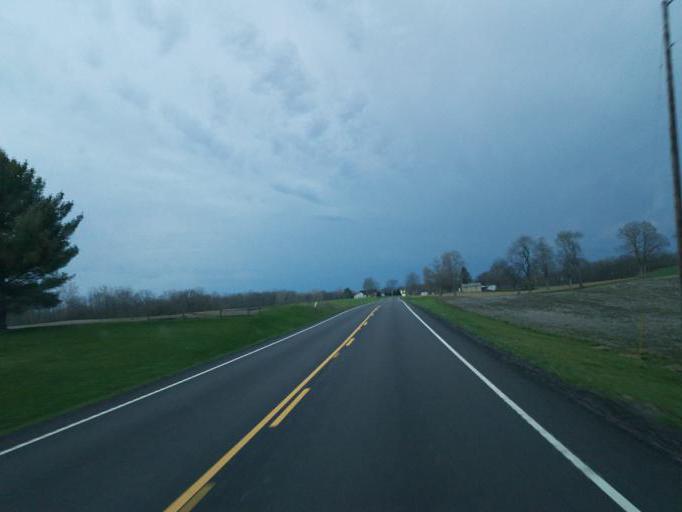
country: US
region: Ohio
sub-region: Knox County
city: Fredericktown
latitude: 40.4627
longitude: -82.6293
